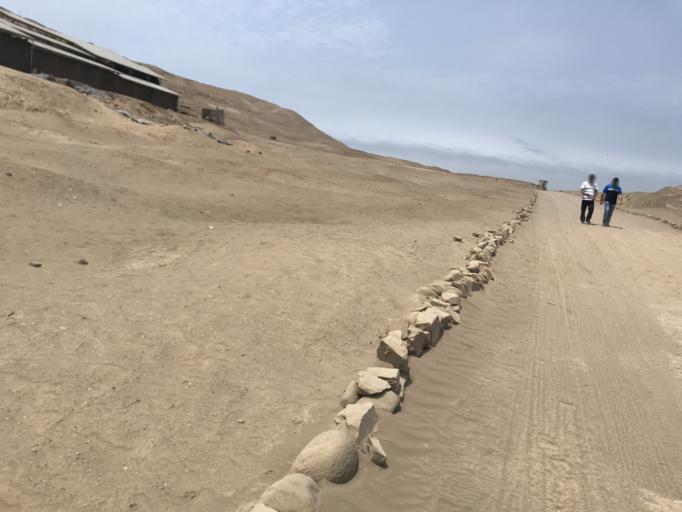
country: PE
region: Lima
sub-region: Lima
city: Punta Hermosa
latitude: -12.2596
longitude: -76.9011
